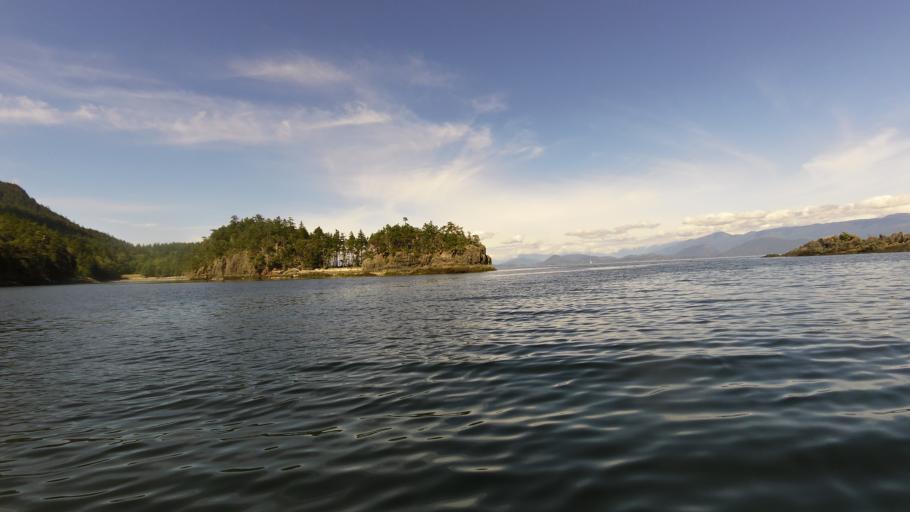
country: CA
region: British Columbia
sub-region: Regional District of Nanaimo
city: Parksville
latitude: 49.5146
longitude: -124.1344
